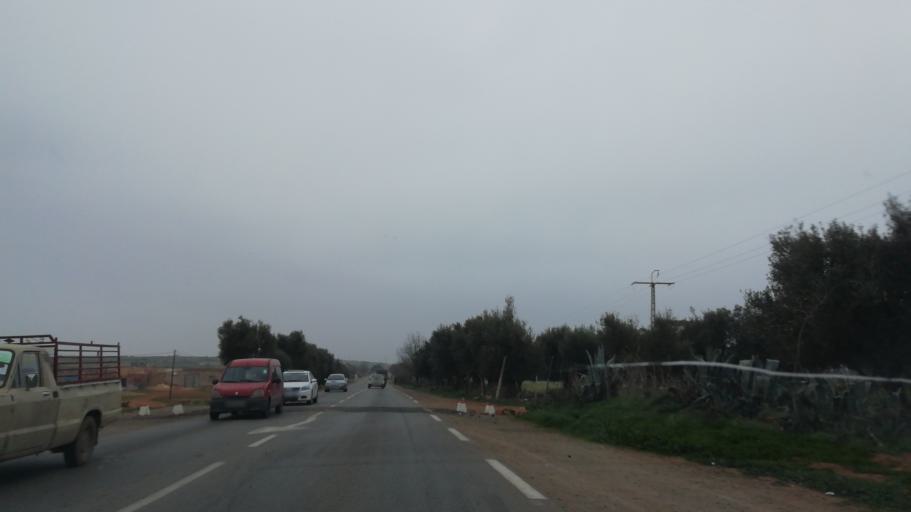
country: DZ
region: Mascara
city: Mascara
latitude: 35.3073
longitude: 0.4094
